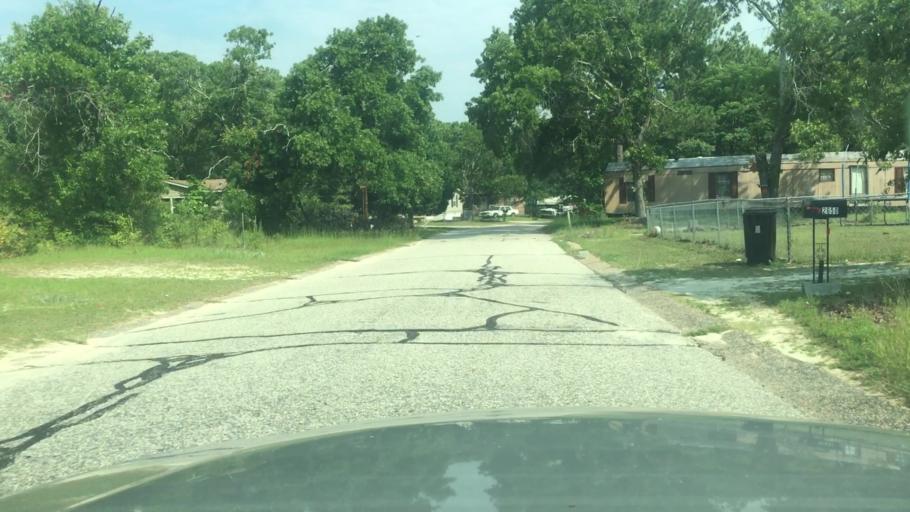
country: US
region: North Carolina
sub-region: Cumberland County
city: Hope Mills
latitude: 35.0017
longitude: -78.9505
